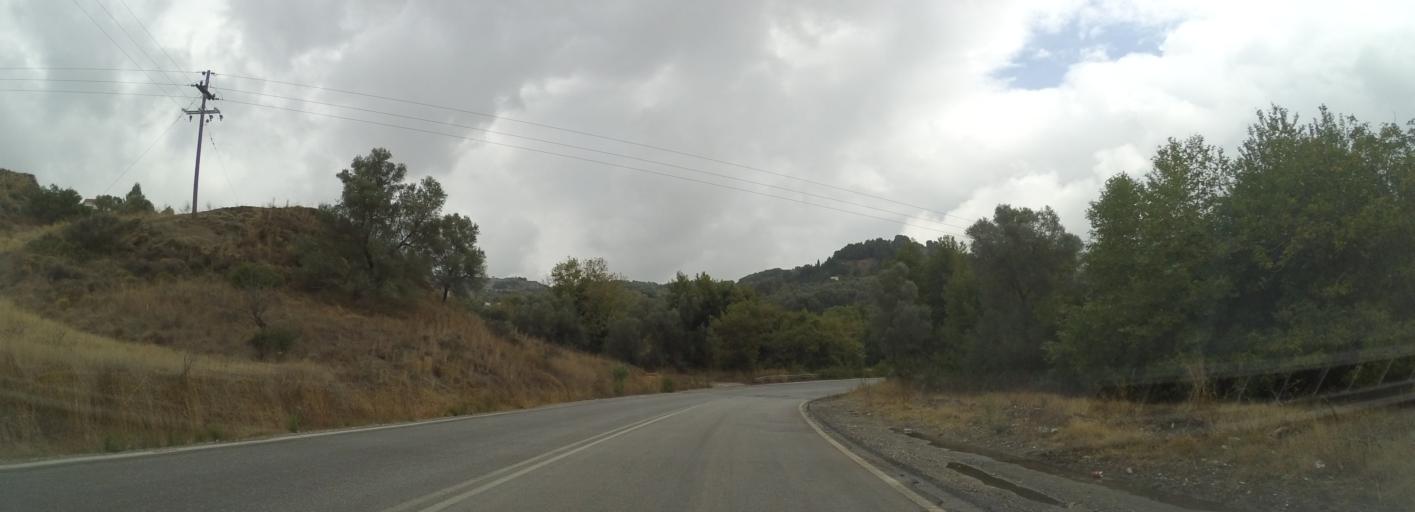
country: GR
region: Crete
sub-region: Nomos Rethymnis
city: Agia Foteini
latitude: 35.2212
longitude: 24.5092
